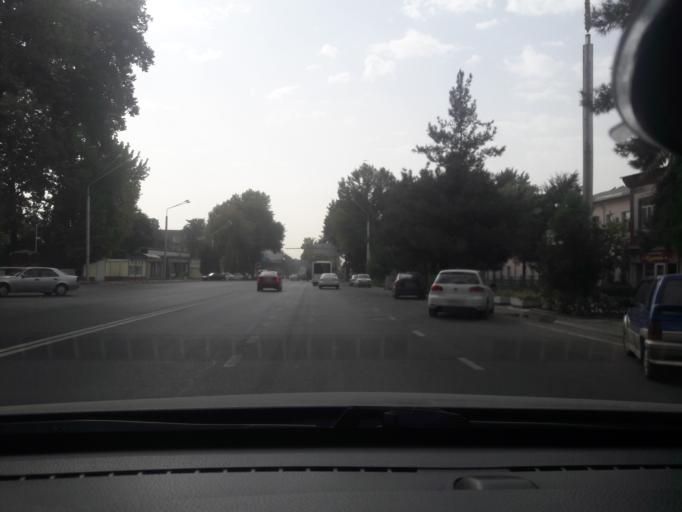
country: TJ
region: Dushanbe
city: Dushanbe
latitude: 38.5766
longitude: 68.8036
